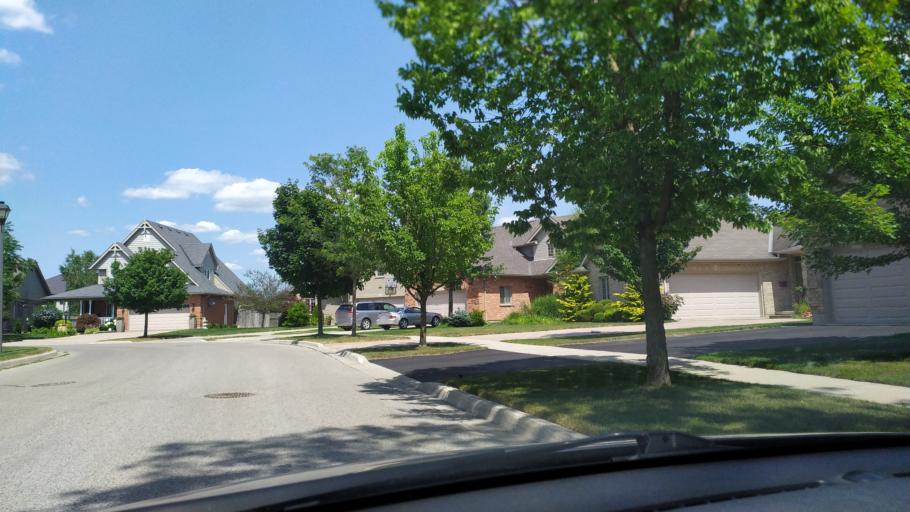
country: CA
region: Ontario
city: Stratford
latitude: 43.3629
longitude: -81.0025
